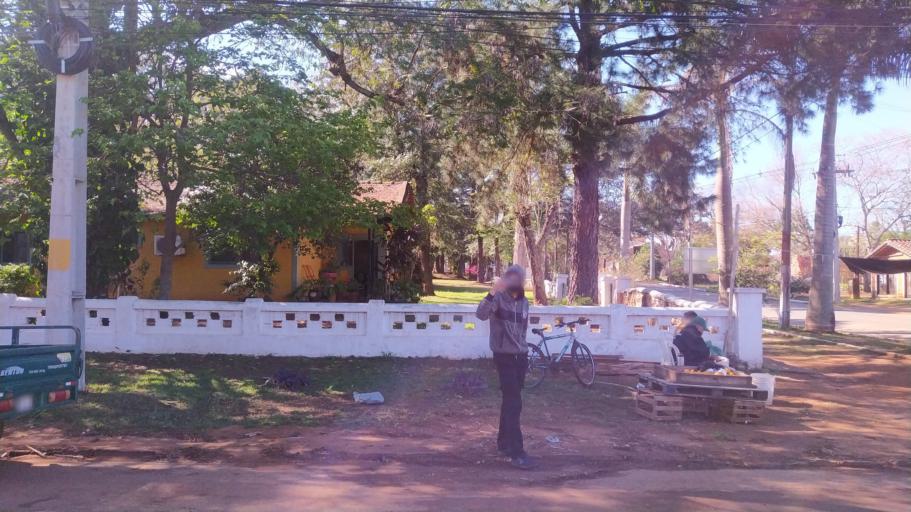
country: PY
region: Misiones
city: San Juan Bautista
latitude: -26.6704
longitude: -57.1369
